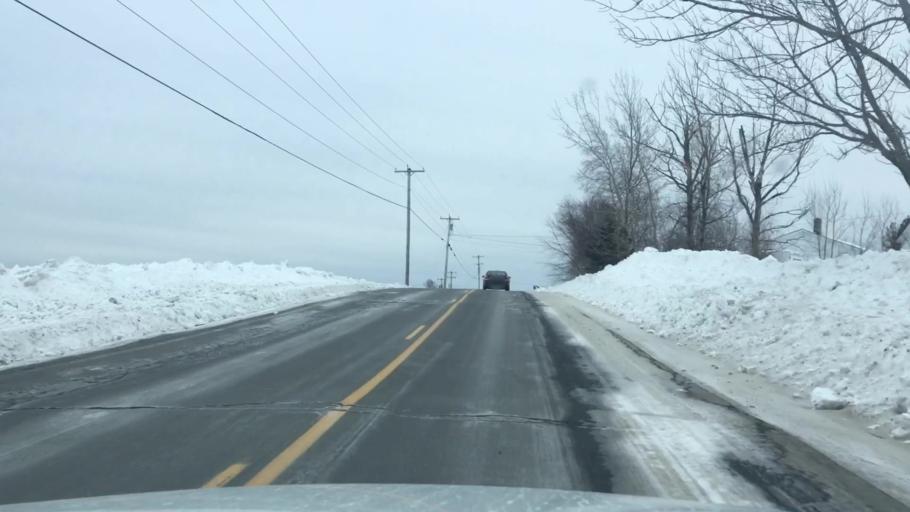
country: US
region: Maine
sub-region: Penobscot County
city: Garland
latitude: 44.9782
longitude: -69.0899
